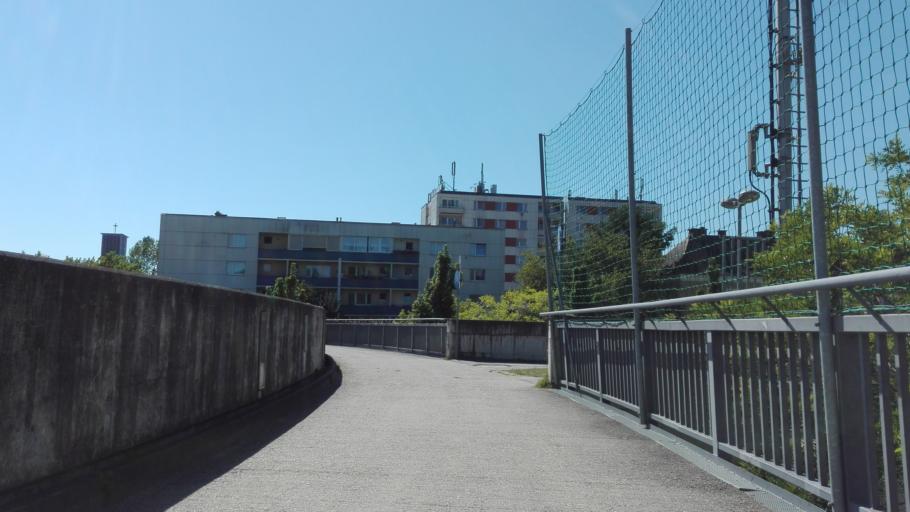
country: AT
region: Upper Austria
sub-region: Linz Stadt
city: Linz
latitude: 48.2727
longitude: 14.2955
